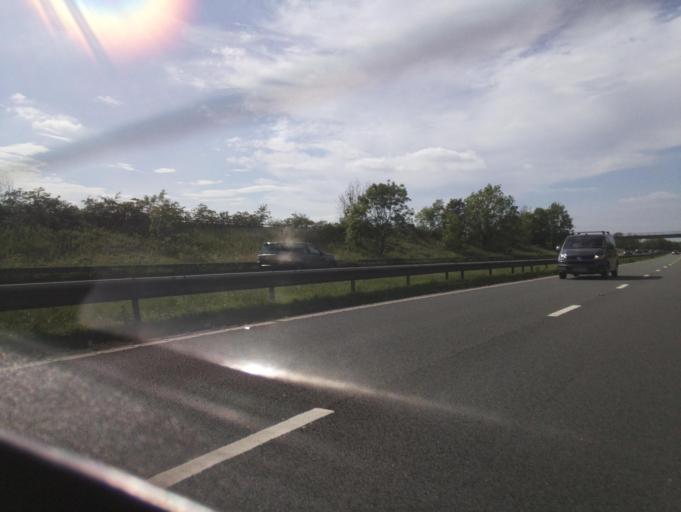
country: GB
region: England
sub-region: Lancashire
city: Chorley
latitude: 53.6446
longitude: -2.6028
